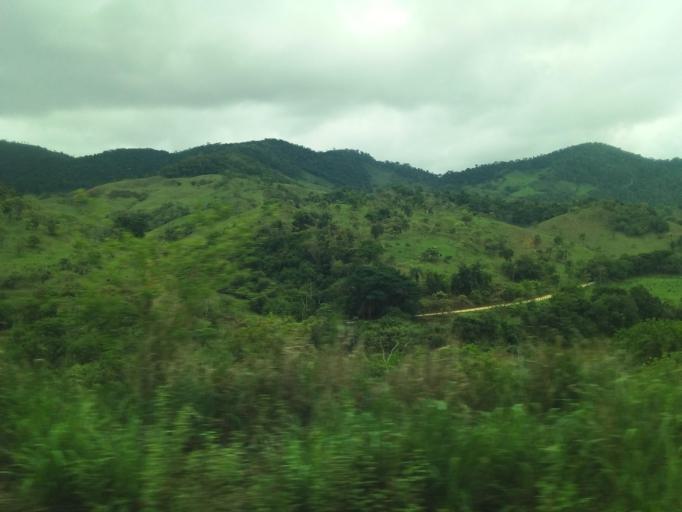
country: BR
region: Minas Gerais
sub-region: Nova Era
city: Nova Era
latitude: -19.6663
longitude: -42.8914
